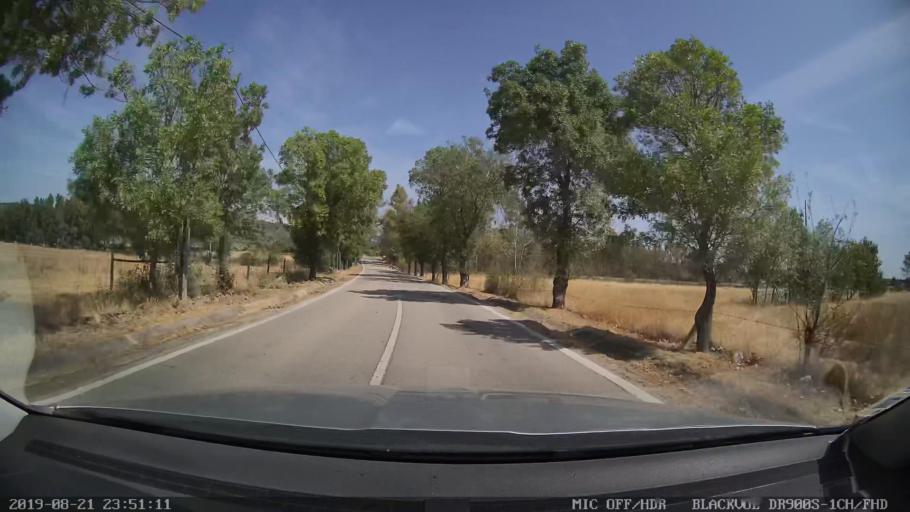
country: PT
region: Castelo Branco
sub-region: Idanha-A-Nova
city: Idanha-a-Nova
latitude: 39.8989
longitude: -7.2354
